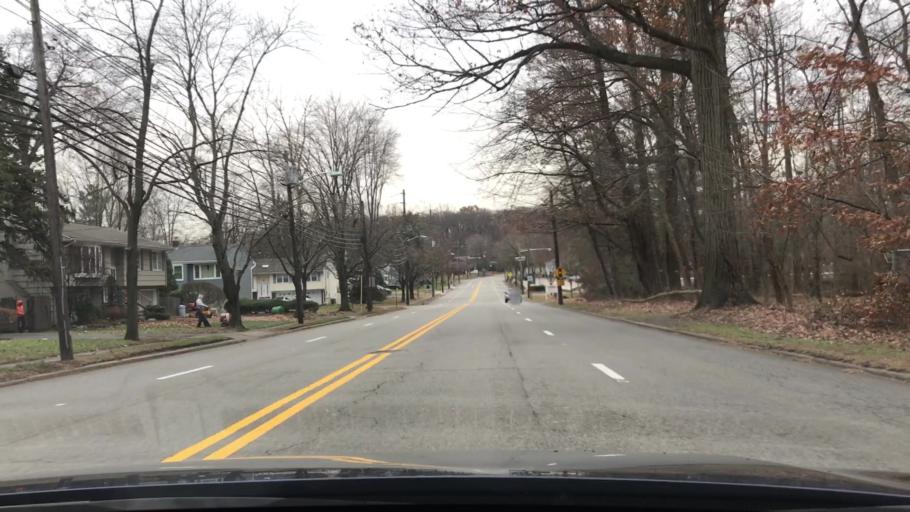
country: US
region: New Jersey
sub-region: Bergen County
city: Paramus
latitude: 40.9529
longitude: -74.0582
